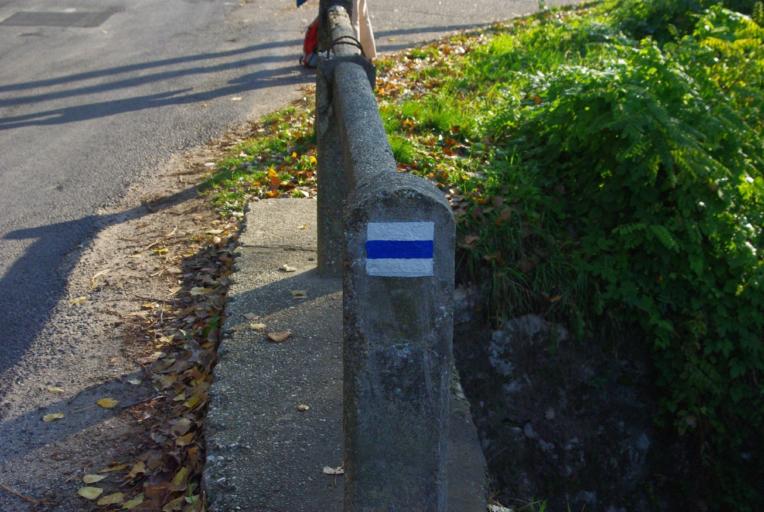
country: HU
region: Komarom-Esztergom
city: Kesztolc
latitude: 47.7180
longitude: 18.7792
